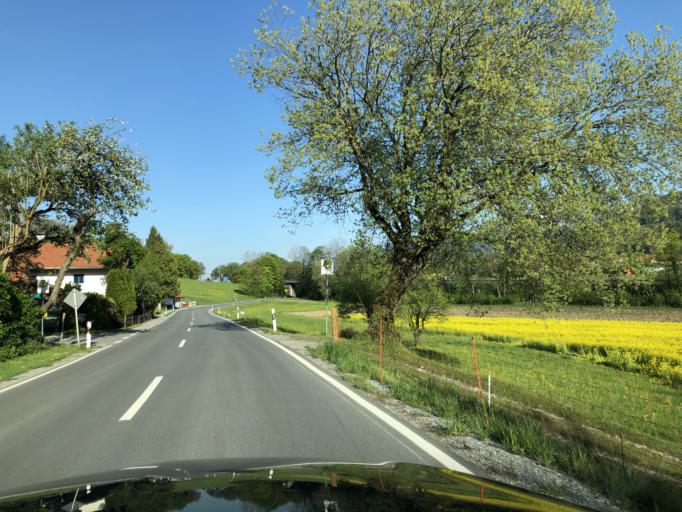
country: DE
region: Bavaria
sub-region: Upper Bavaria
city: Frasdorf
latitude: 47.8045
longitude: 12.2737
